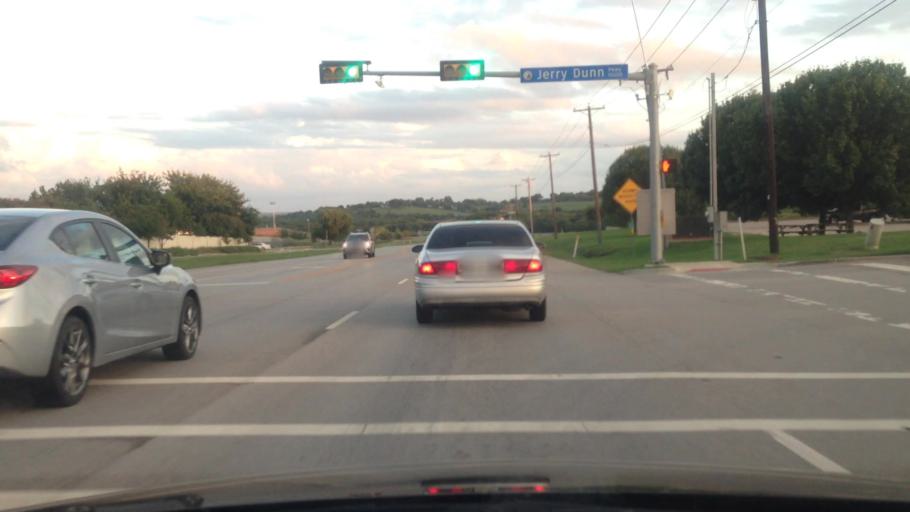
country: US
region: Texas
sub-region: Tarrant County
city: Benbrook
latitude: 32.6668
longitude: -97.4894
